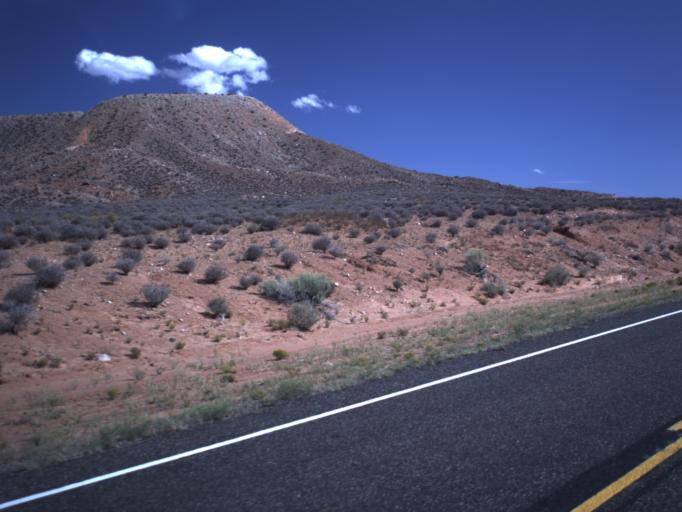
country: US
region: Utah
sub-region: Wayne County
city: Loa
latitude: 38.1525
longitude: -110.6205
